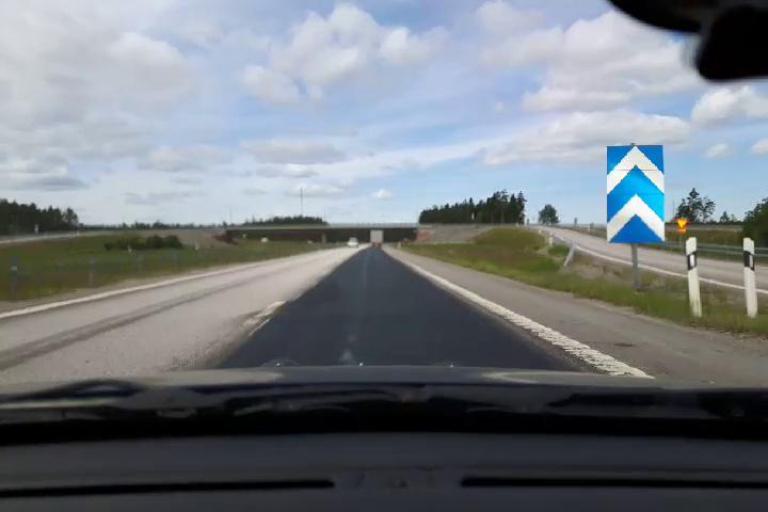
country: SE
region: Uppsala
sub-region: Tierps Kommun
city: Tierp
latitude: 60.4377
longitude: 17.4224
